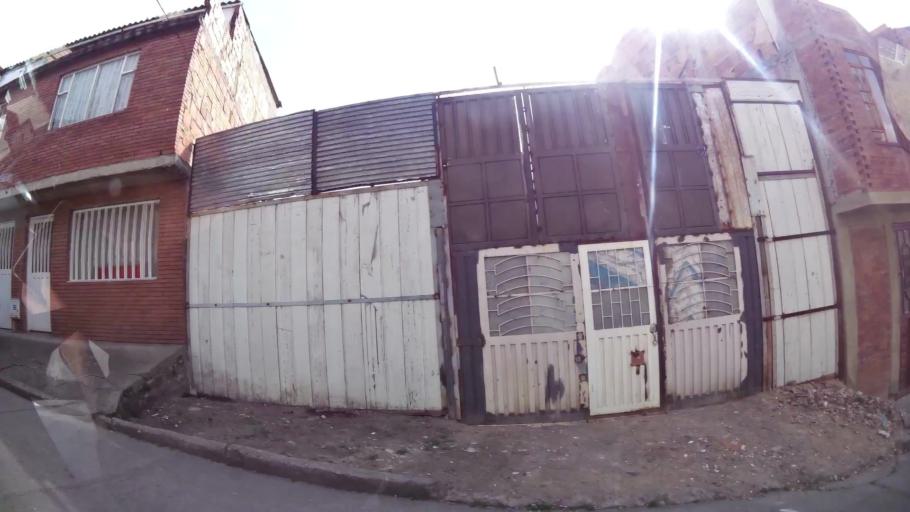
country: CO
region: Bogota D.C.
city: Bogota
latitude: 4.5461
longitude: -74.0902
